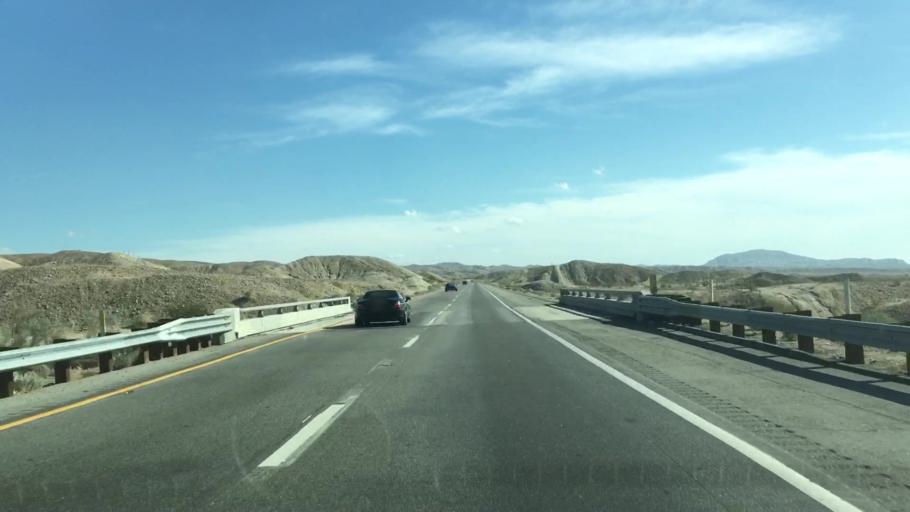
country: US
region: California
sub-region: Riverside County
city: Coachella
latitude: 33.7045
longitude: -116.1335
